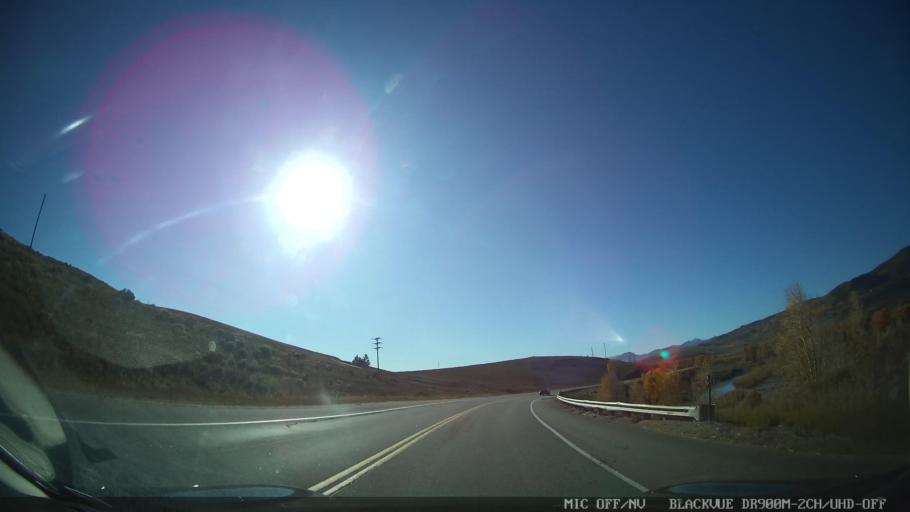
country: US
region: Colorado
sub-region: Grand County
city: Granby
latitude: 40.1071
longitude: -105.9755
